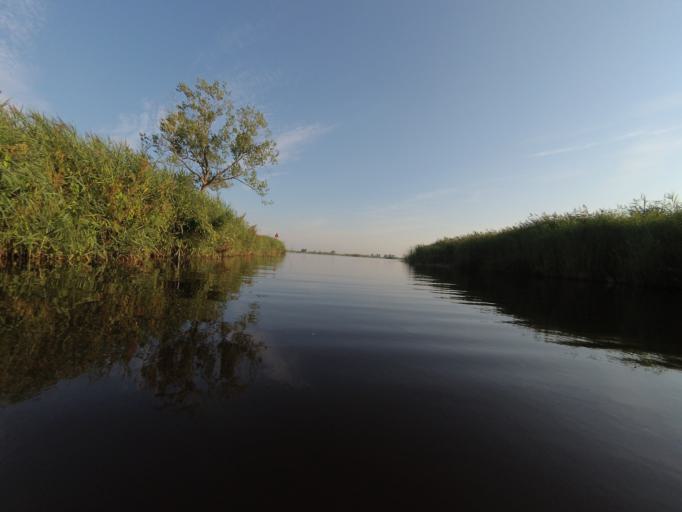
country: NL
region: Overijssel
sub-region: Gemeente Steenwijkerland
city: Sint Jansklooster
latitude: 52.6754
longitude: 6.0309
